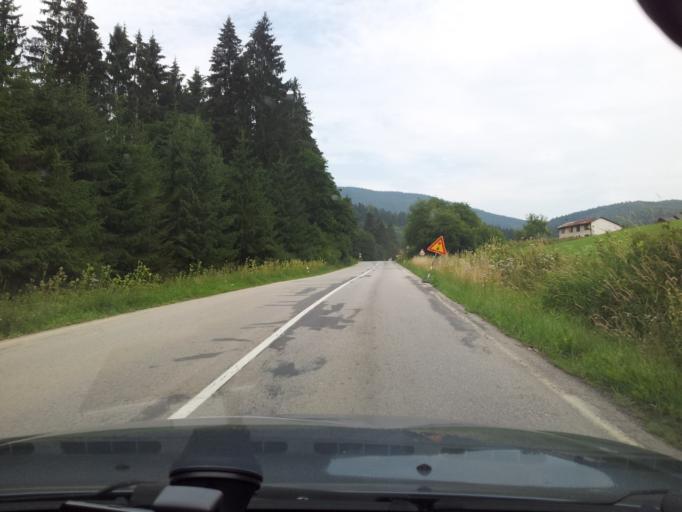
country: SK
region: Zilinsky
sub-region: Okres Dolny Kubin
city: Dolny Kubin
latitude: 49.2777
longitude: 19.3473
